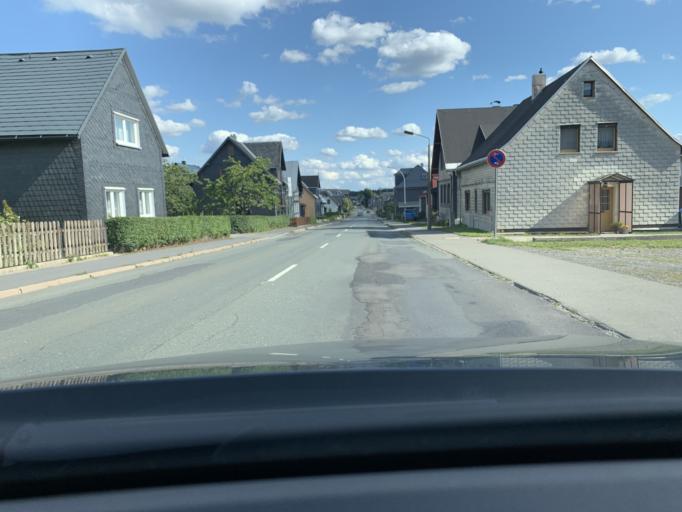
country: DE
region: Thuringia
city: Neuhaus am Rennweg
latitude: 50.4993
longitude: 11.1516
